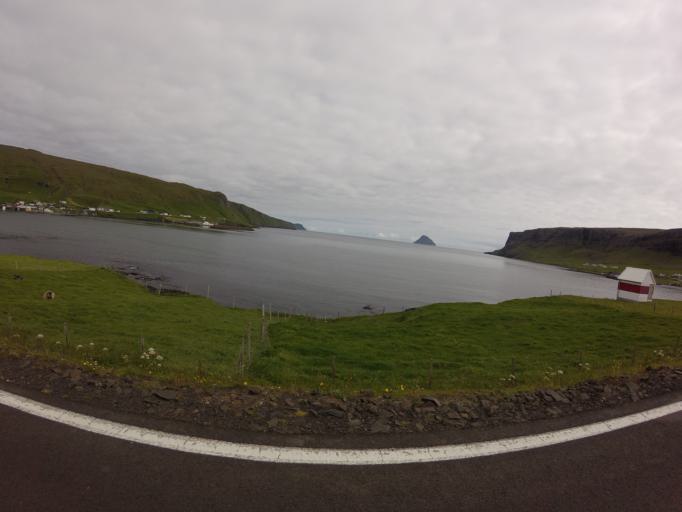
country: FO
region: Suduroy
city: Tvoroyri
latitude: 61.5964
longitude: -6.9463
